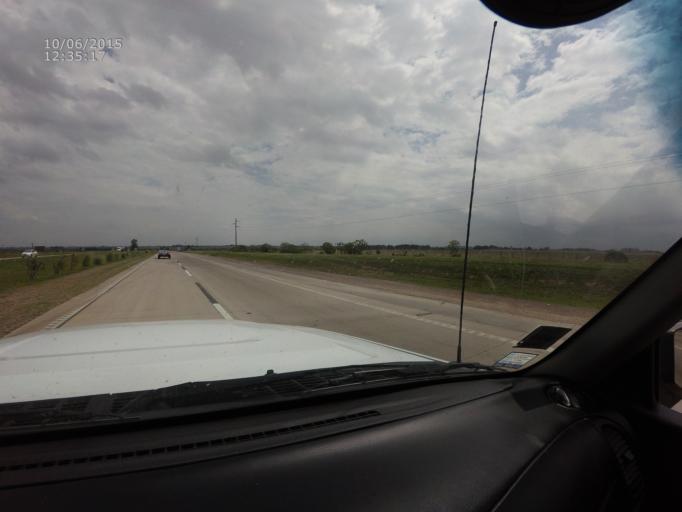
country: AR
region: Santa Fe
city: Carcarana
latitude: -32.8755
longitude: -61.1743
